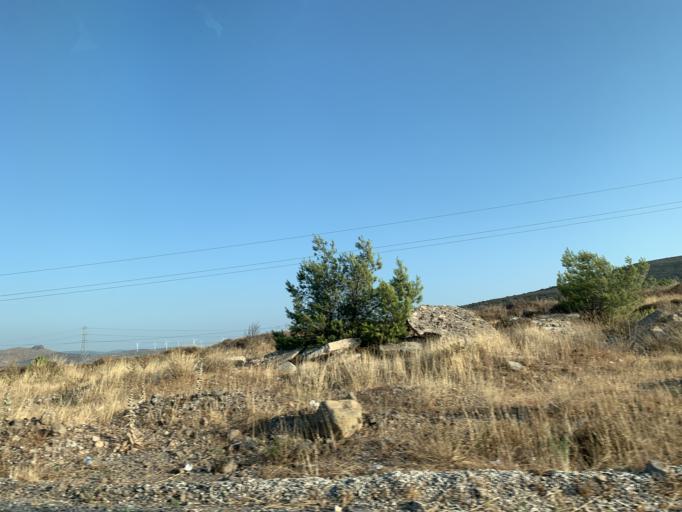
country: TR
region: Izmir
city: Alacati
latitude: 38.2762
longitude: 26.4136
